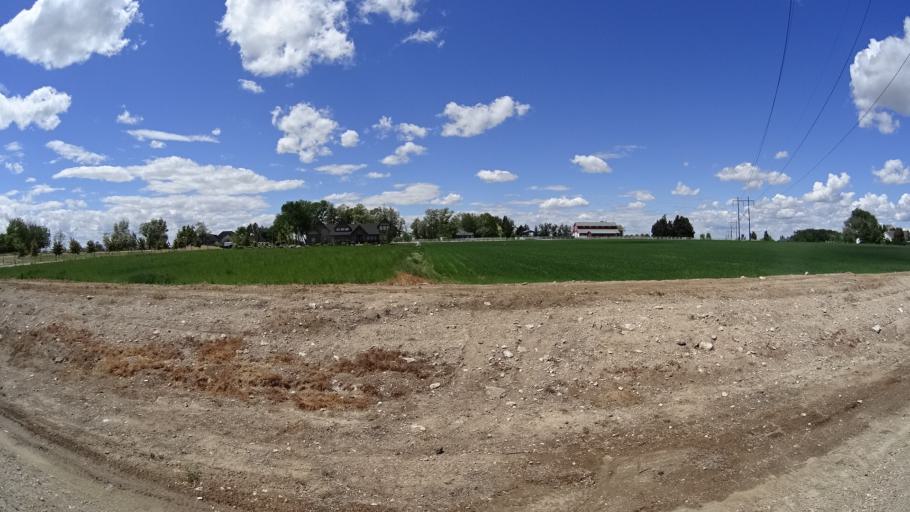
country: US
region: Idaho
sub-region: Ada County
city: Meridian
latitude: 43.5704
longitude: -116.4533
